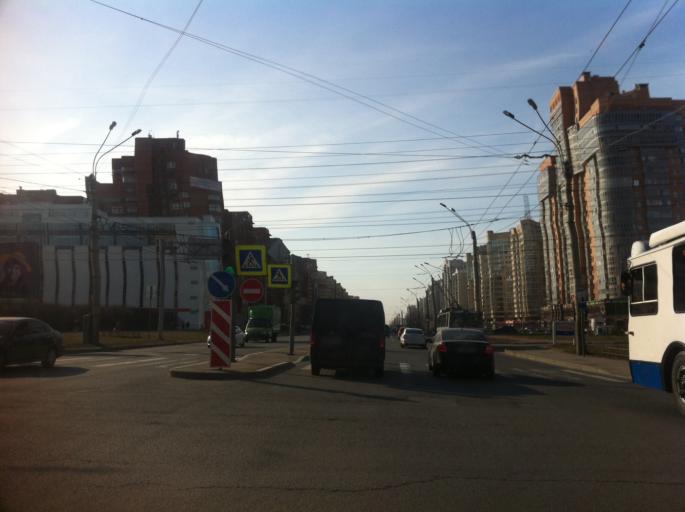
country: RU
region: St.-Petersburg
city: Uritsk
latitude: 59.8563
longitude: 30.2024
